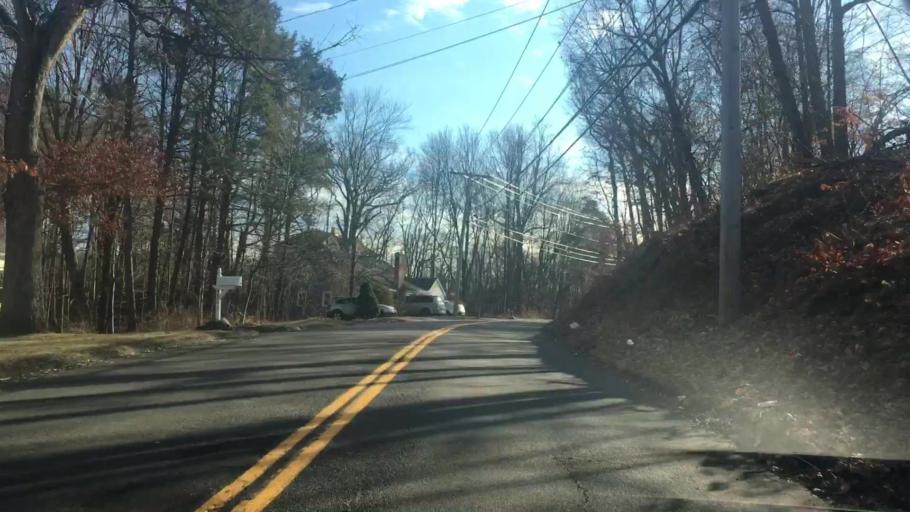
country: US
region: Connecticut
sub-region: Middlesex County
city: Middletown
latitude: 41.5186
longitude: -72.6489
